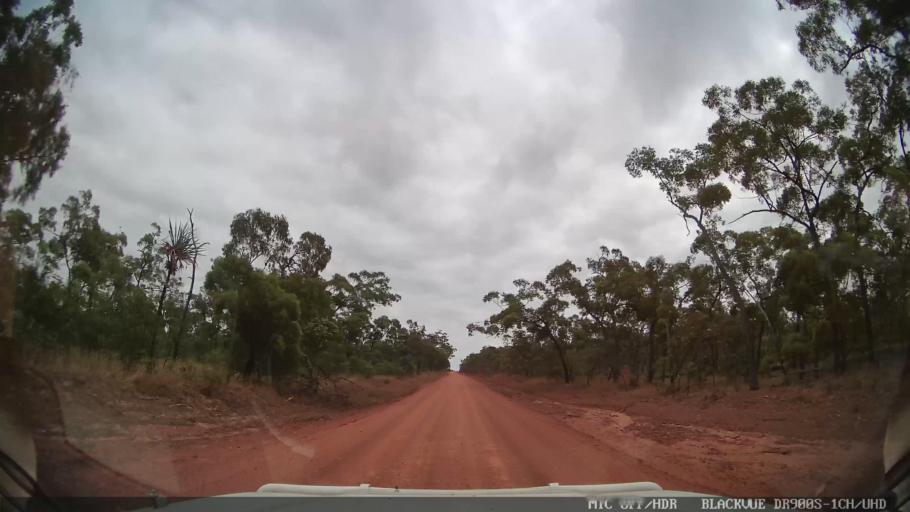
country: AU
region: Queensland
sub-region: Cook
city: Cooktown
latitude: -15.2654
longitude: 144.9503
